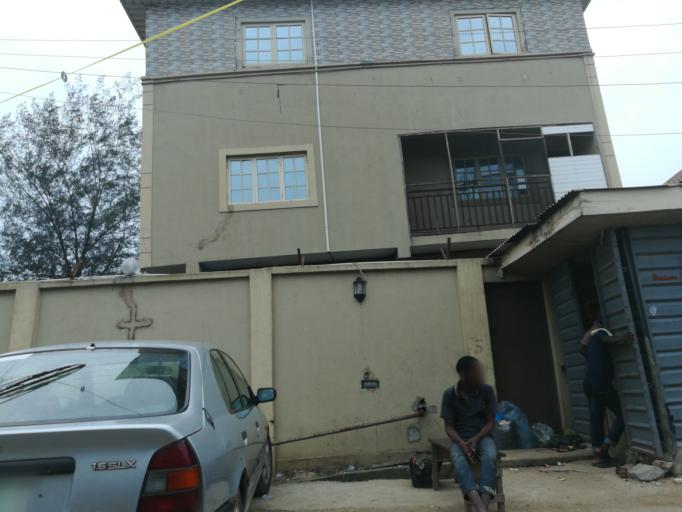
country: NG
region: Lagos
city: Makoko
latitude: 6.5038
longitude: 3.3890
